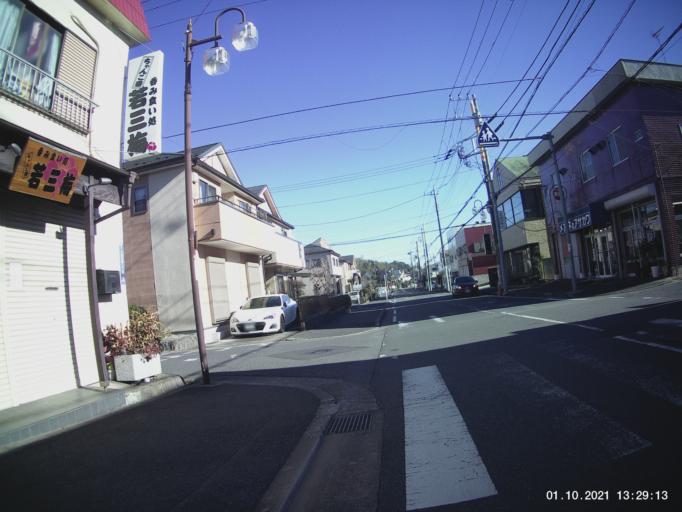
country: JP
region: Chiba
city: Yotsukaido
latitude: 35.5979
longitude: 140.2171
